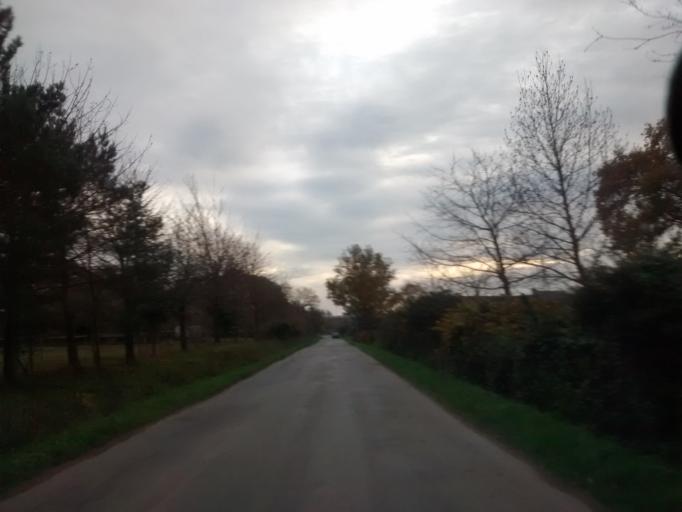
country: FR
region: Brittany
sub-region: Departement d'Ille-et-Vilaine
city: Cesson-Sevigne
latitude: 48.1233
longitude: -1.5834
